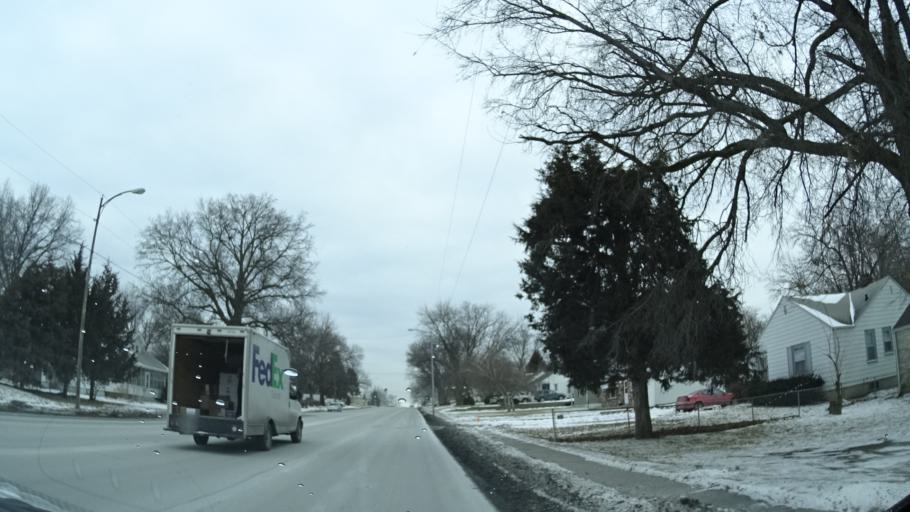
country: US
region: Nebraska
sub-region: Douglas County
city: Omaha
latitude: 41.2324
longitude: -95.9758
